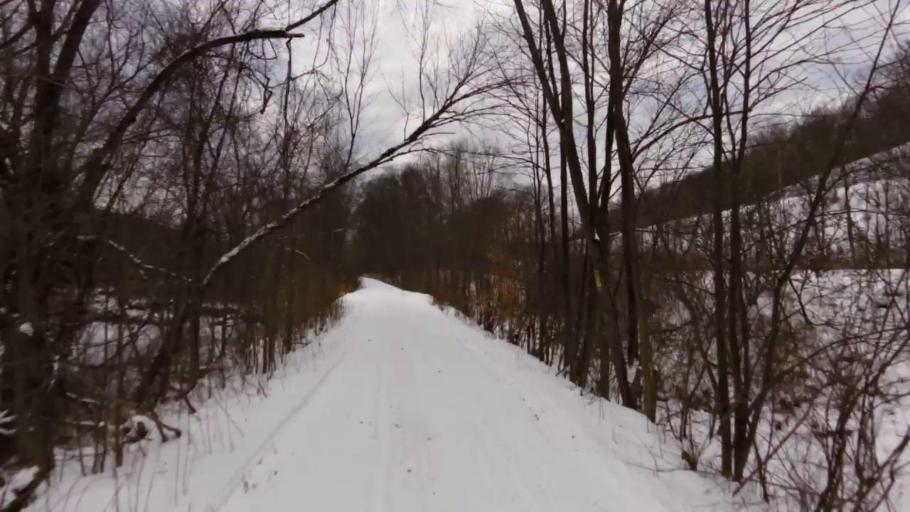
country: US
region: Pennsylvania
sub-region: McKean County
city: Foster Brook
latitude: 42.0605
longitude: -78.6377
